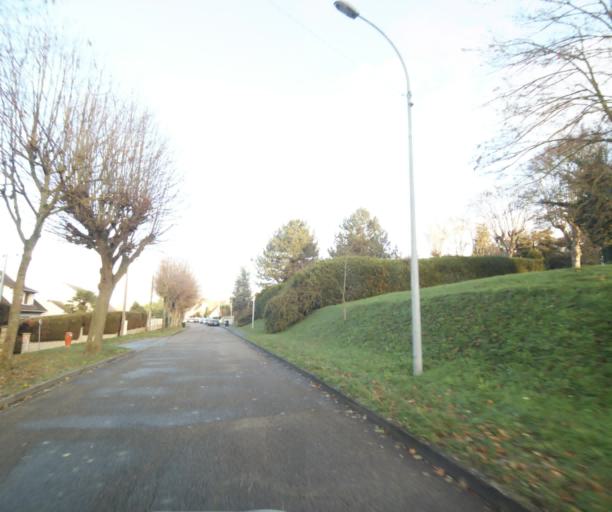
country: FR
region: Ile-de-France
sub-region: Departement des Yvelines
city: Meulan-en-Yvelines
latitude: 49.0116
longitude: 1.9115
